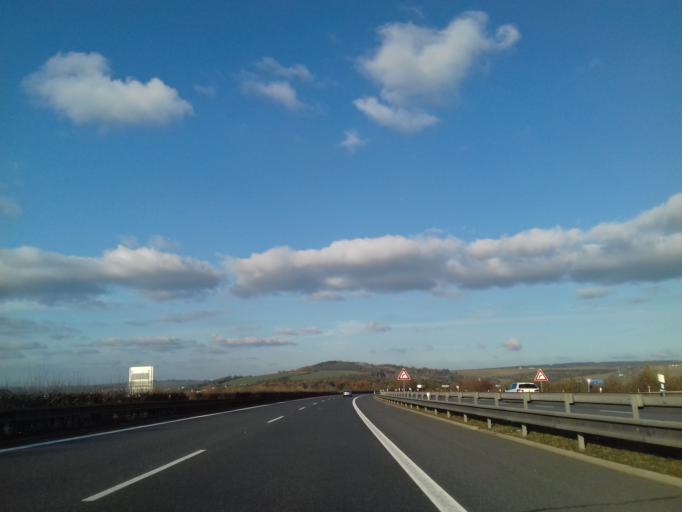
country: CZ
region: Plzensky
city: Stary Plzenec
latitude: 49.6993
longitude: 13.4315
